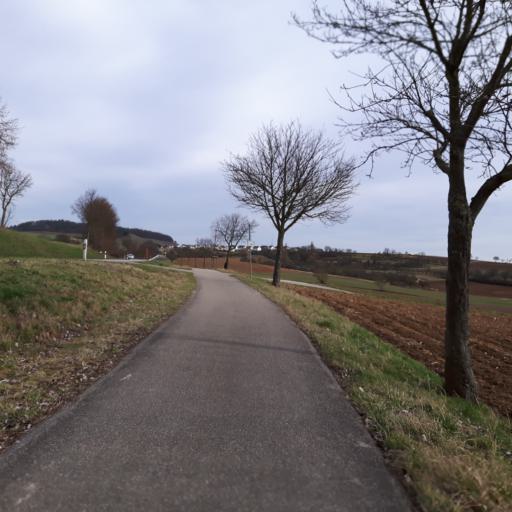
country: DE
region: Baden-Wuerttemberg
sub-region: Regierungsbezirk Stuttgart
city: Abstatt
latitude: 49.0500
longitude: 9.2876
